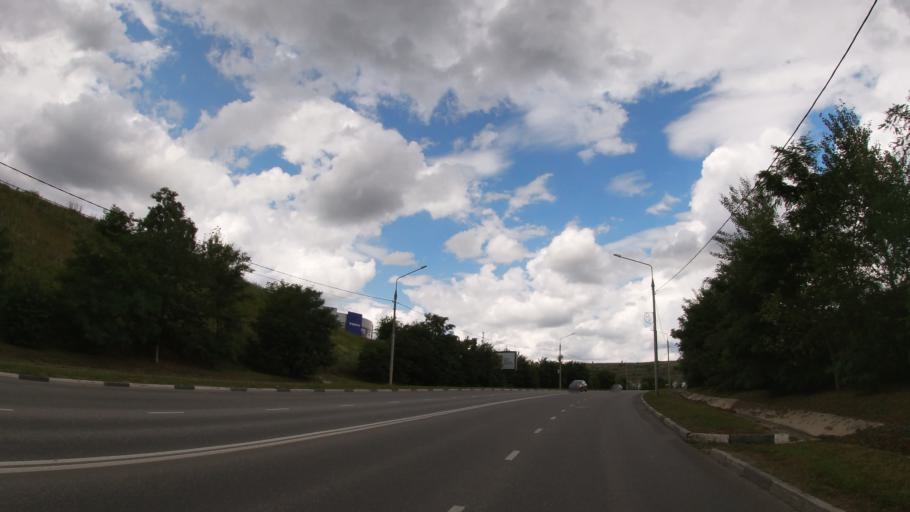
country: RU
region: Belgorod
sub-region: Belgorodskiy Rayon
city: Belgorod
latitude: 50.6108
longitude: 36.6125
